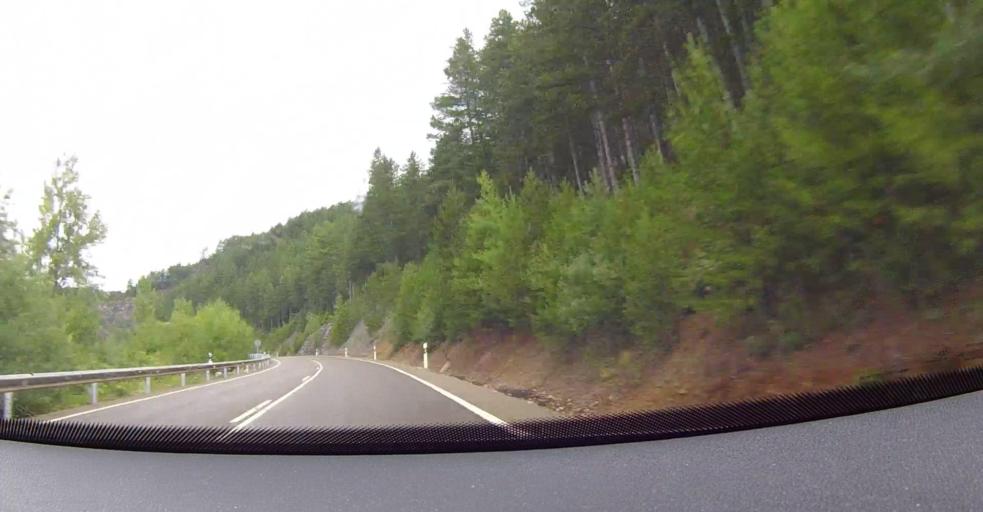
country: ES
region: Castille and Leon
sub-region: Provincia de Leon
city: Cistierna
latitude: 42.8224
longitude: -5.1202
